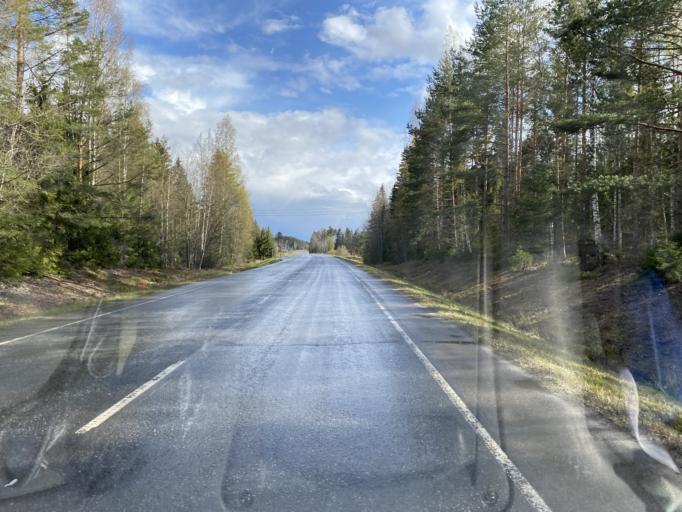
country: FI
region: Pirkanmaa
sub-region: Etelae-Pirkanmaa
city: Viiala
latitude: 61.2150
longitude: 23.7353
